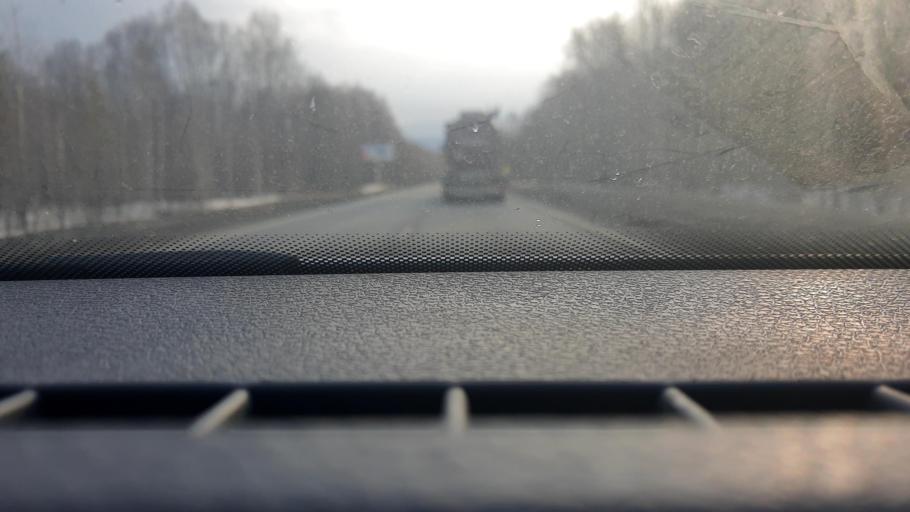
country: RU
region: Chelyabinsk
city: Asha
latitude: 54.8837
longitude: 57.2704
